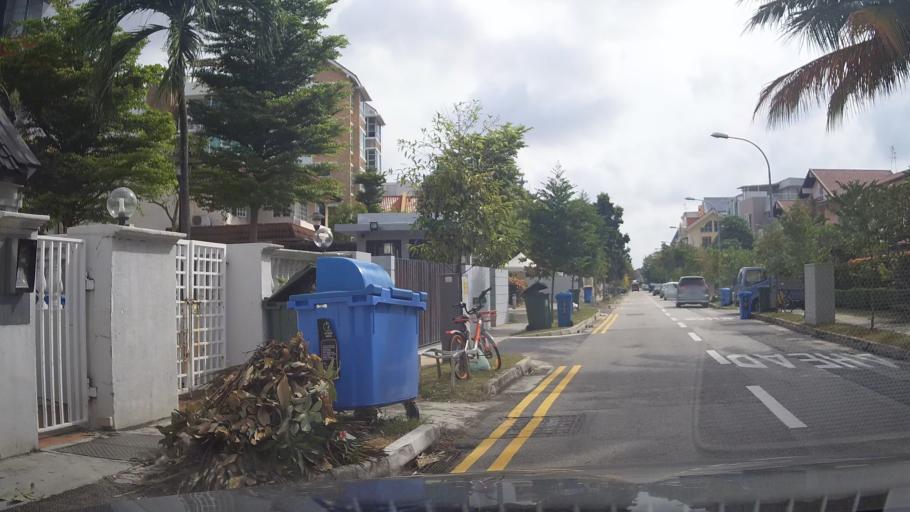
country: SG
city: Singapore
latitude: 1.3121
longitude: 103.9124
